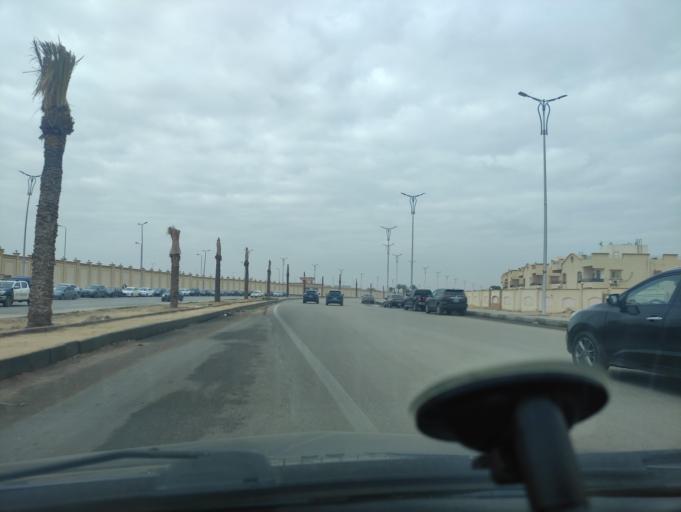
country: EG
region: Muhafazat al Qalyubiyah
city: Al Khankah
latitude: 30.0520
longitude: 31.4247
